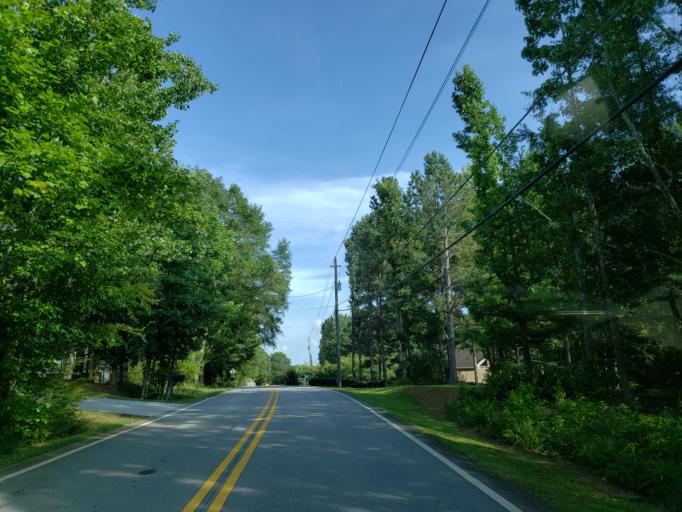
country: US
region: Georgia
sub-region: Paulding County
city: Hiram
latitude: 33.9161
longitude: -84.7185
